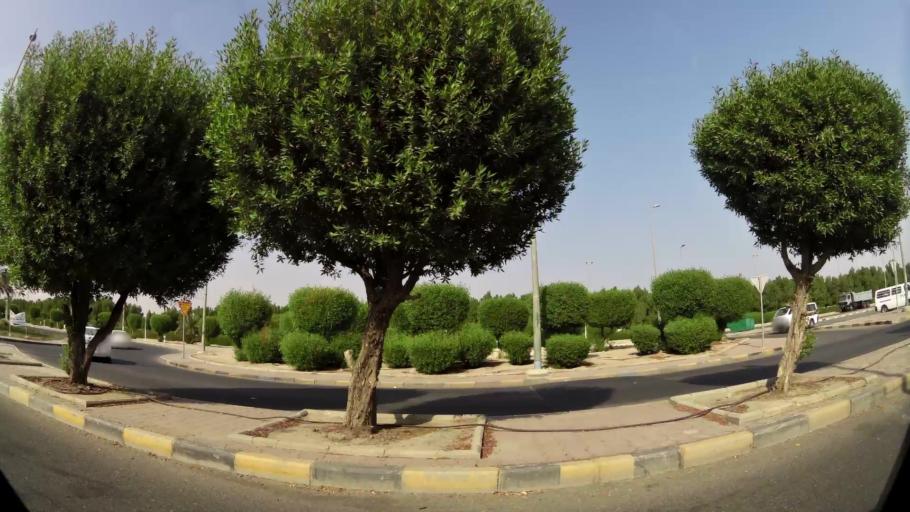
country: KW
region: Muhafazat al Jahra'
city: Al Jahra'
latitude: 29.3472
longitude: 47.6966
